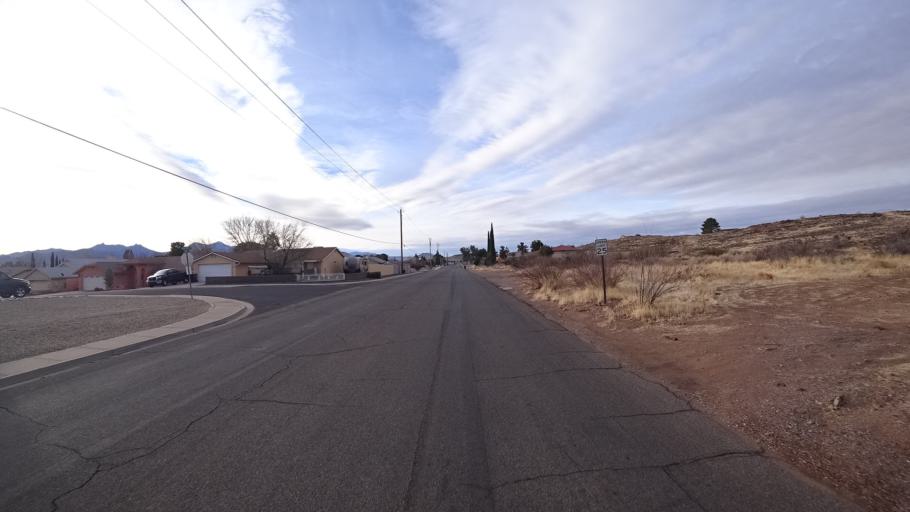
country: US
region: Arizona
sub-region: Mohave County
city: New Kingman-Butler
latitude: 35.2331
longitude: -114.0403
